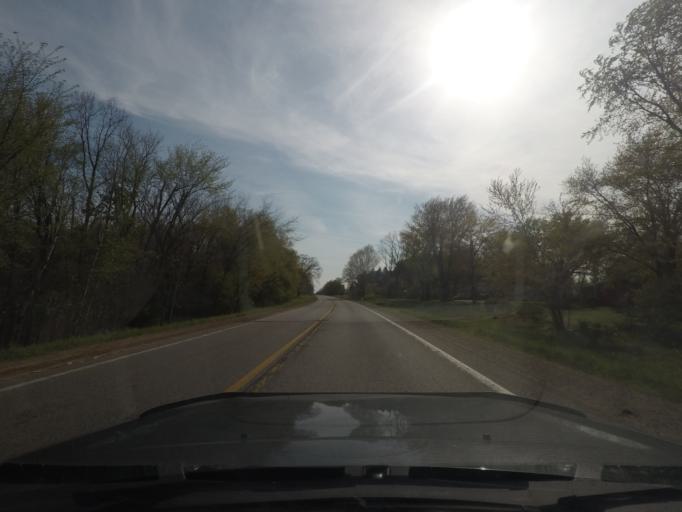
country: US
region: Michigan
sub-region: Berrien County
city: Buchanan
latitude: 41.8041
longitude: -86.4004
